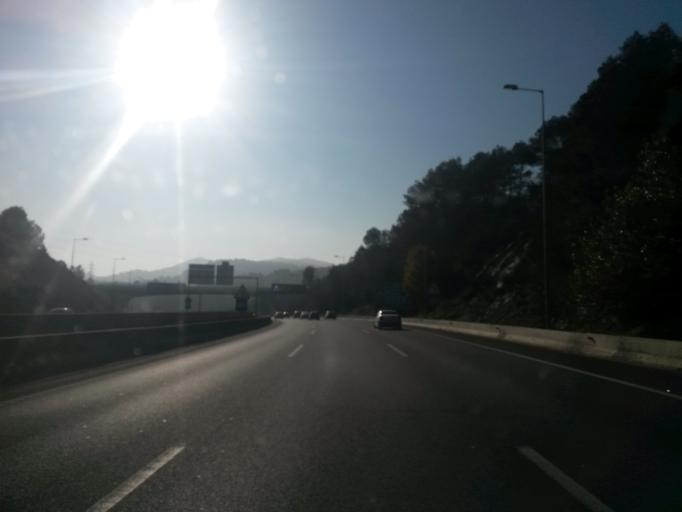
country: ES
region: Catalonia
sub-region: Provincia de Barcelona
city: Montcada i Reixac
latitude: 41.4748
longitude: 2.1628
